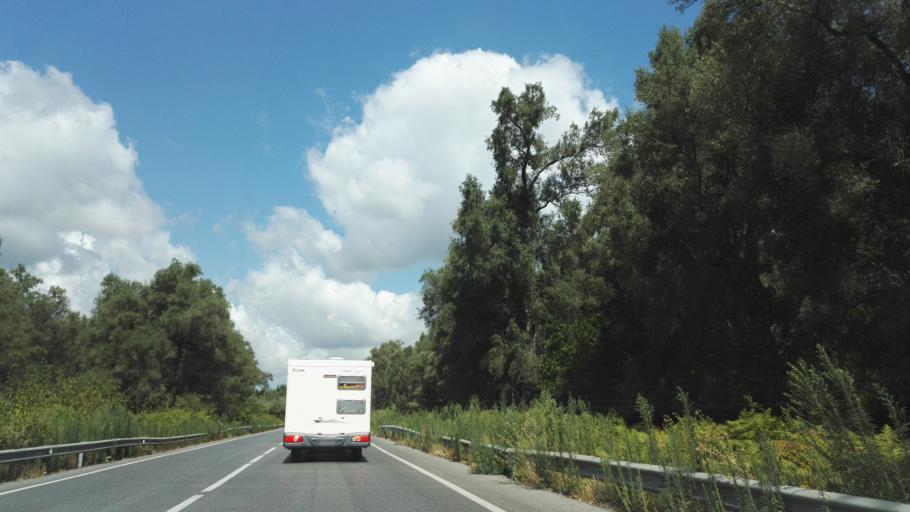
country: IT
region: Calabria
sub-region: Provincia di Reggio Calabria
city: Melicucco
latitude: 38.4244
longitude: 16.0608
